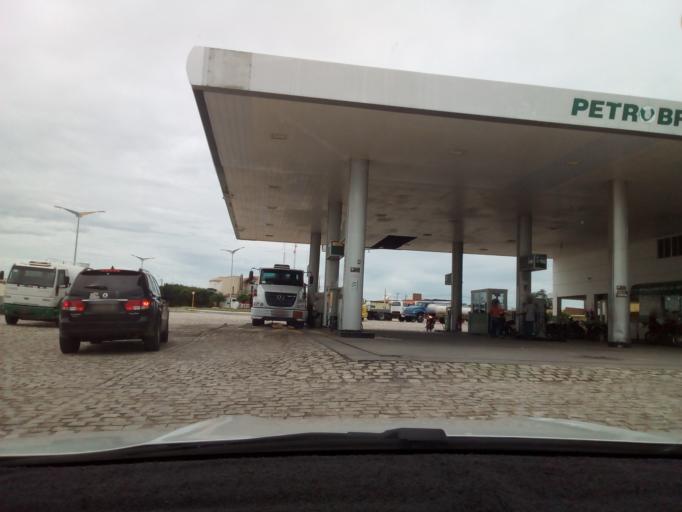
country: BR
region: Rio Grande do Norte
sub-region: Caraubas
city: Caraubas
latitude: -5.7859
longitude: -37.5603
